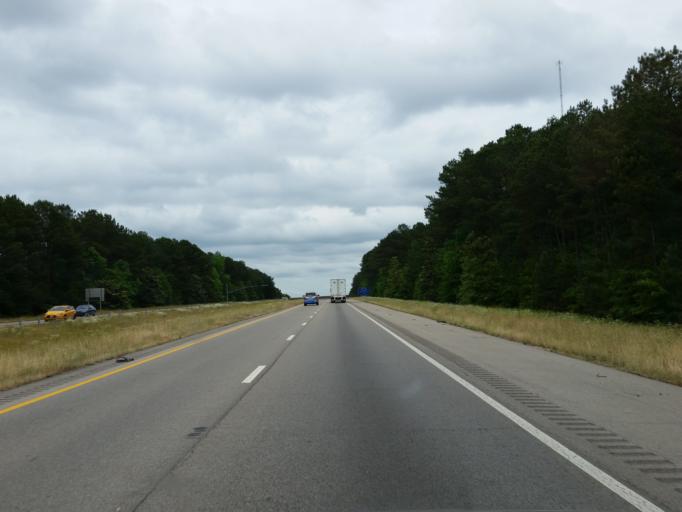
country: US
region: Alabama
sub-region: Sumter County
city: York
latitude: 32.4434
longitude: -88.4210
